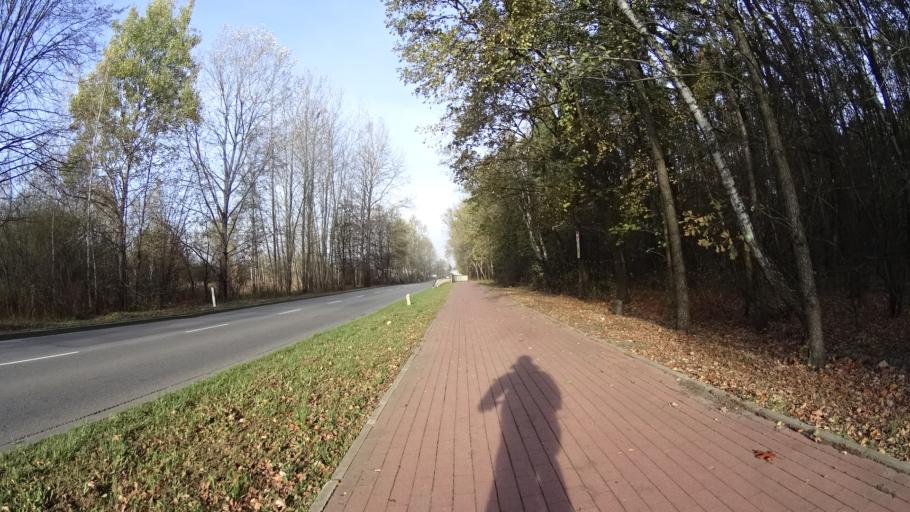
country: PL
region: Masovian Voivodeship
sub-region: Powiat warszawski zachodni
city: Babice
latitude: 52.2699
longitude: 20.8613
